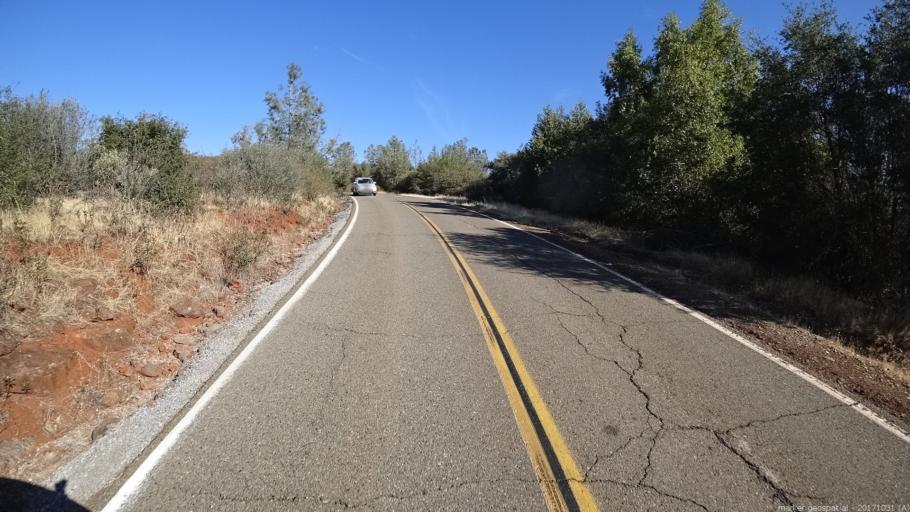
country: US
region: California
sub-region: Shasta County
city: Shingletown
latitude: 40.4468
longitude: -121.8761
